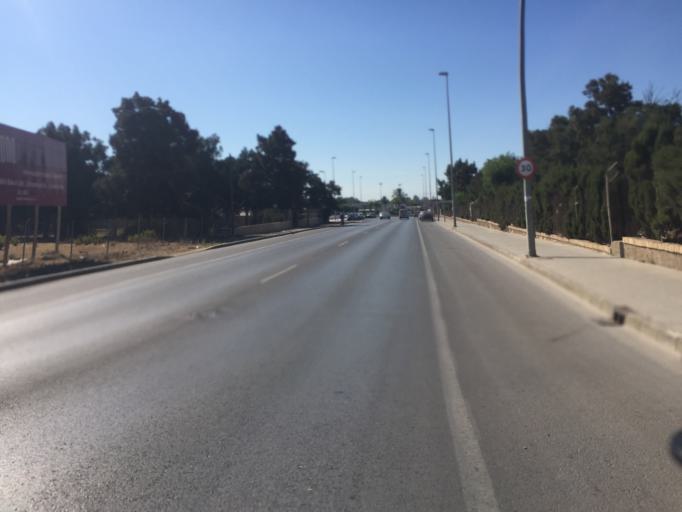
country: ES
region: Andalusia
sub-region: Provincia de Cadiz
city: Chiclana de la Frontera
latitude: 36.4023
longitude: -6.1672
